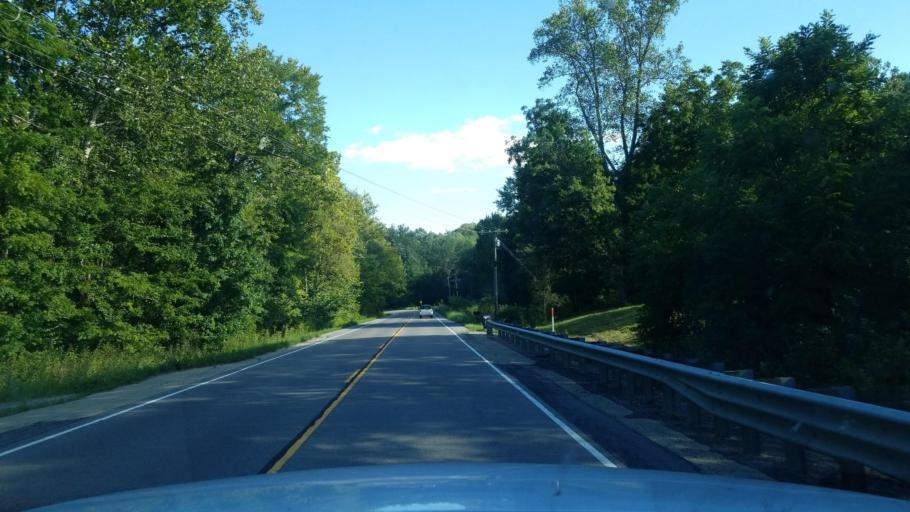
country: US
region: Illinois
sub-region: Saline County
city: Harrisburg
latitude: 37.5903
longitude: -88.4515
